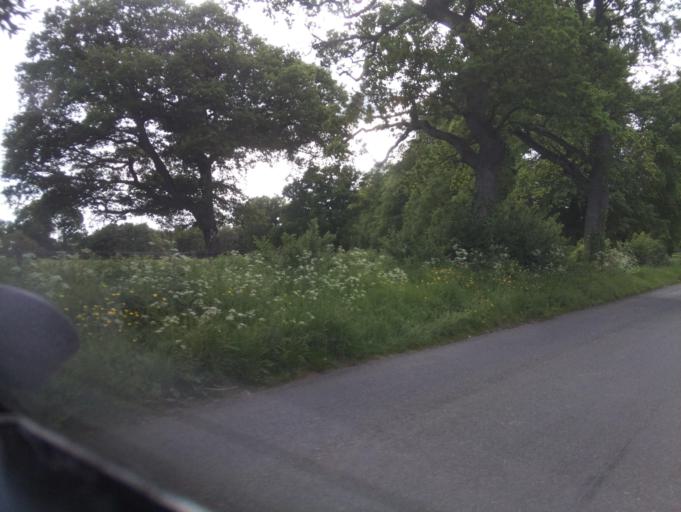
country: GB
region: England
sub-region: Gloucestershire
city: Moreton in Marsh
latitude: 52.0035
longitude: -1.7232
